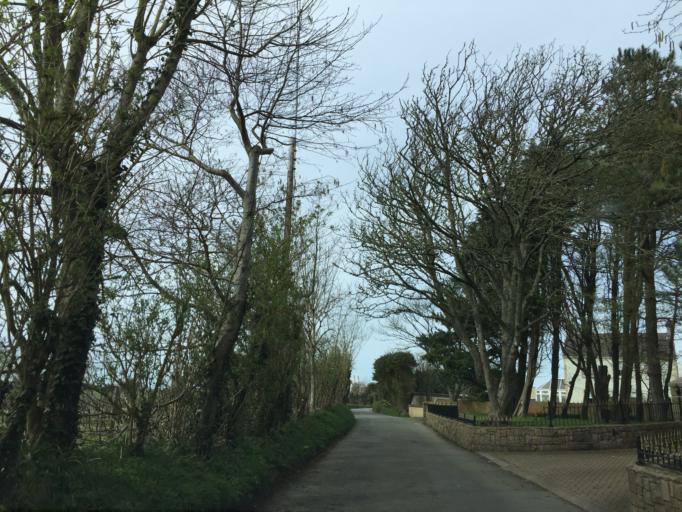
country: JE
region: St Helier
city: Saint Helier
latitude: 49.2471
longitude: -2.1669
